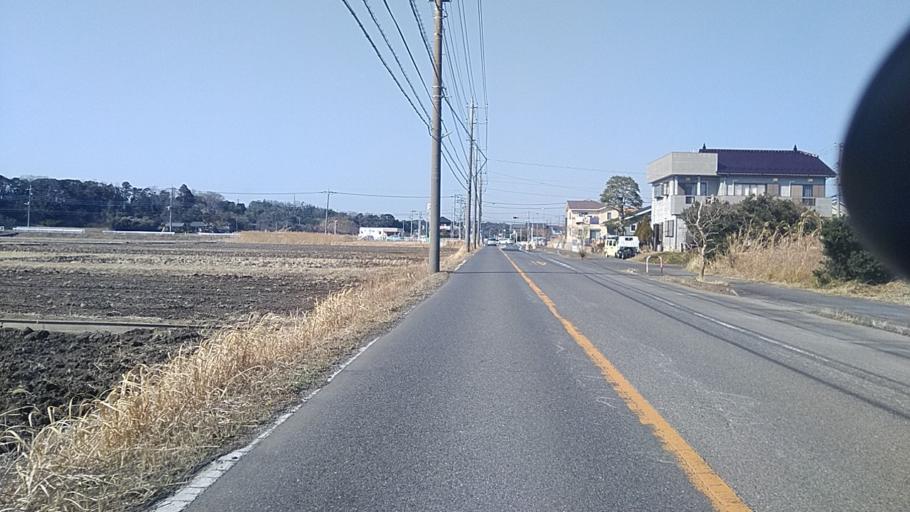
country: JP
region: Chiba
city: Mobara
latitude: 35.4527
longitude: 140.2910
